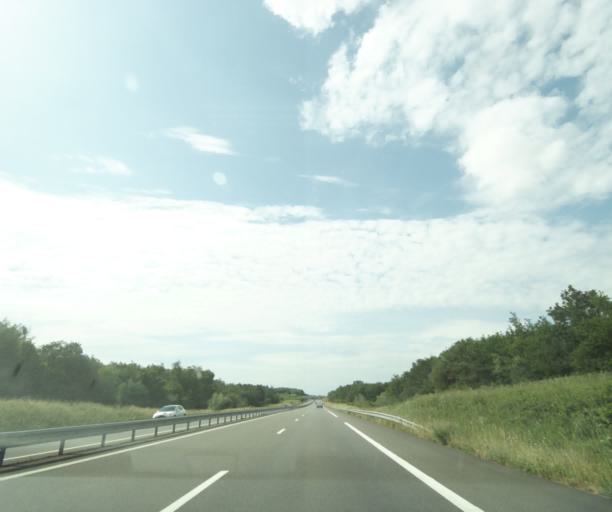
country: FR
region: Pays de la Loire
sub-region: Departement de Maine-et-Loire
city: Maze
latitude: 47.4967
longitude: -0.2775
